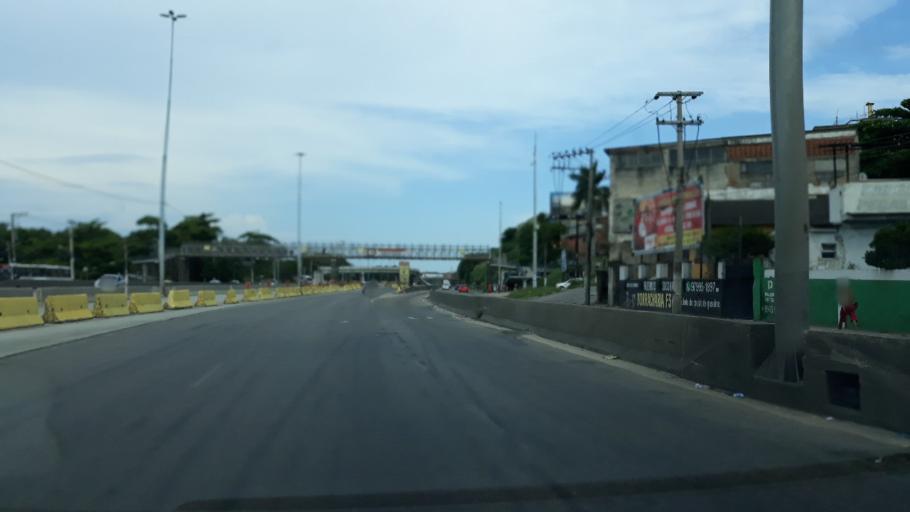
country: BR
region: Rio de Janeiro
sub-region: Duque De Caxias
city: Duque de Caxias
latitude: -22.8145
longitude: -43.2947
